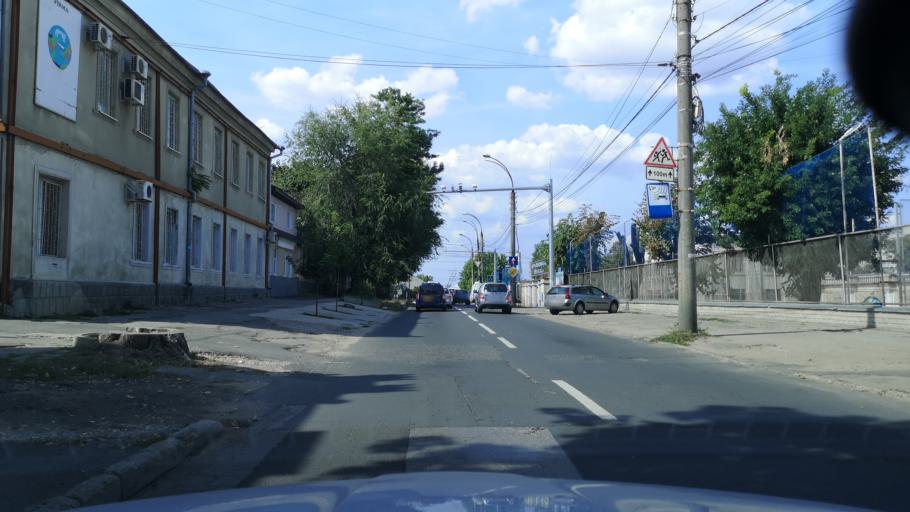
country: MD
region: Chisinau
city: Chisinau
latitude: 47.0257
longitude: 28.8192
